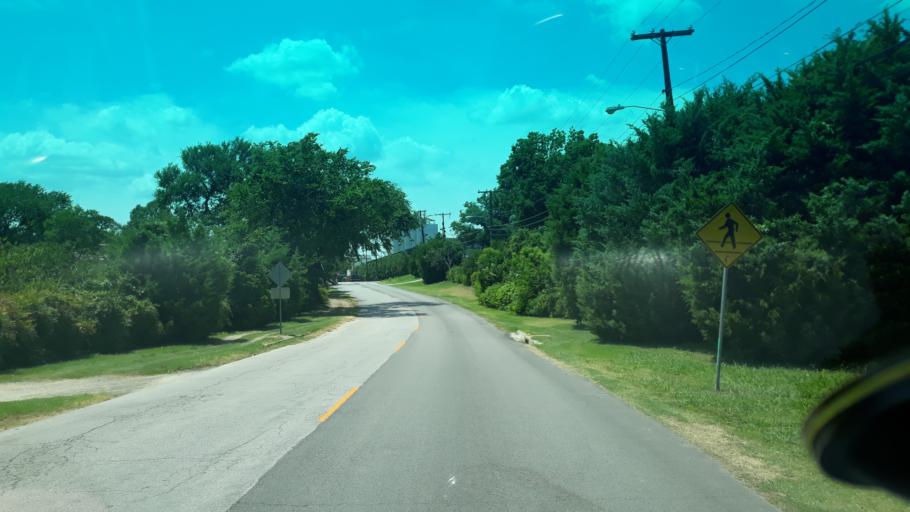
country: US
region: Texas
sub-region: Dallas County
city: Highland Park
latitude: 32.8126
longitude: -96.7488
